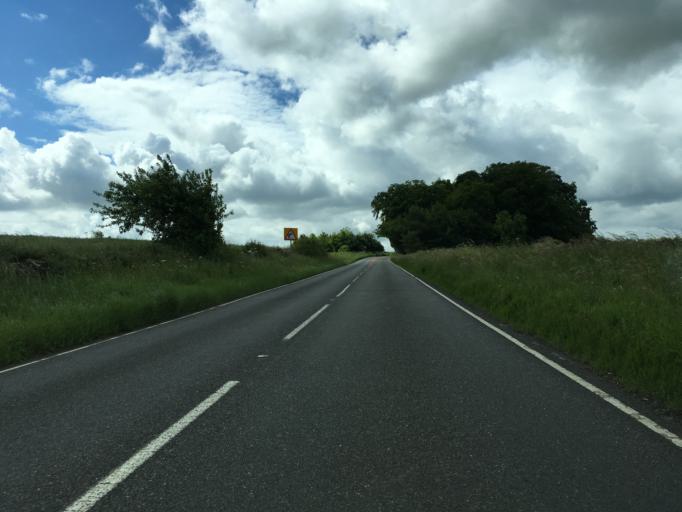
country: GB
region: England
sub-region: Oxfordshire
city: Shipton under Wychwood
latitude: 51.8431
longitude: -1.6024
